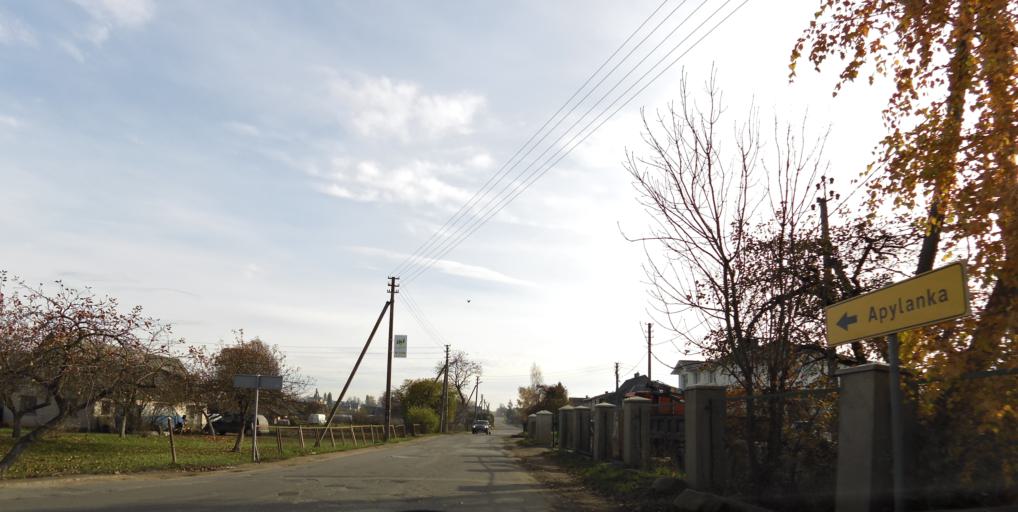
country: LT
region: Vilnius County
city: Pilaite
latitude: 54.7273
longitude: 25.1805
